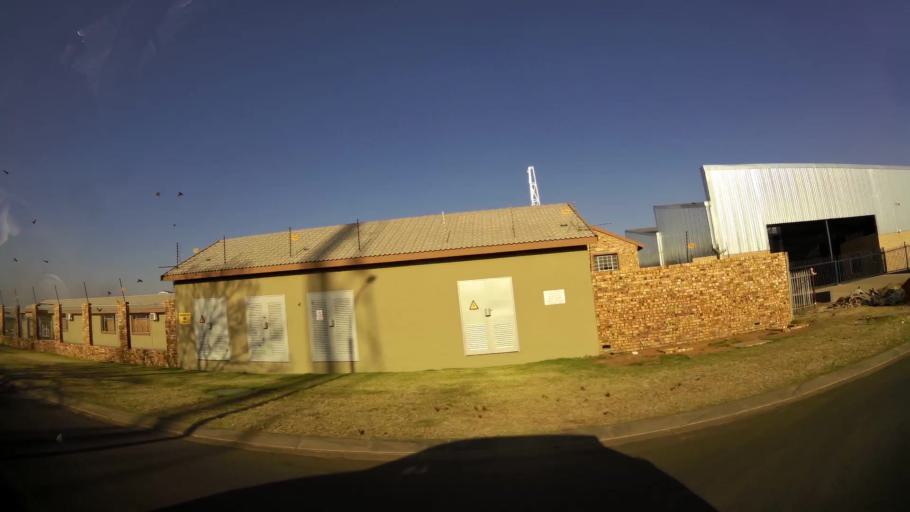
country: ZA
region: Gauteng
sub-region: West Rand District Municipality
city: Randfontein
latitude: -26.1953
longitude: 27.6849
